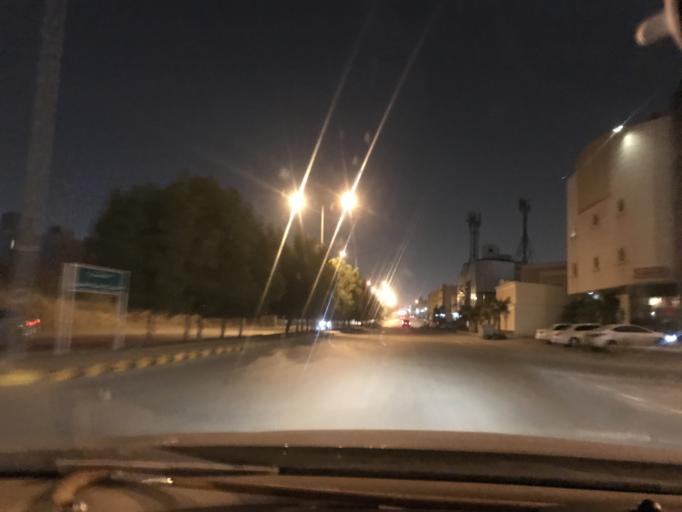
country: SA
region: Ar Riyad
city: Riyadh
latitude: 24.7519
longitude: 46.7543
